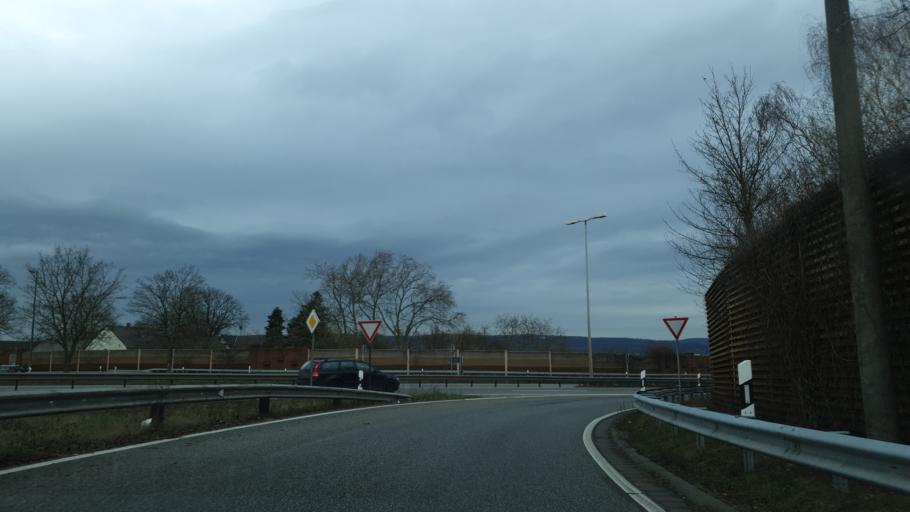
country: DE
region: Rheinland-Pfalz
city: Weissenthurm
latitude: 50.4162
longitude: 7.4483
